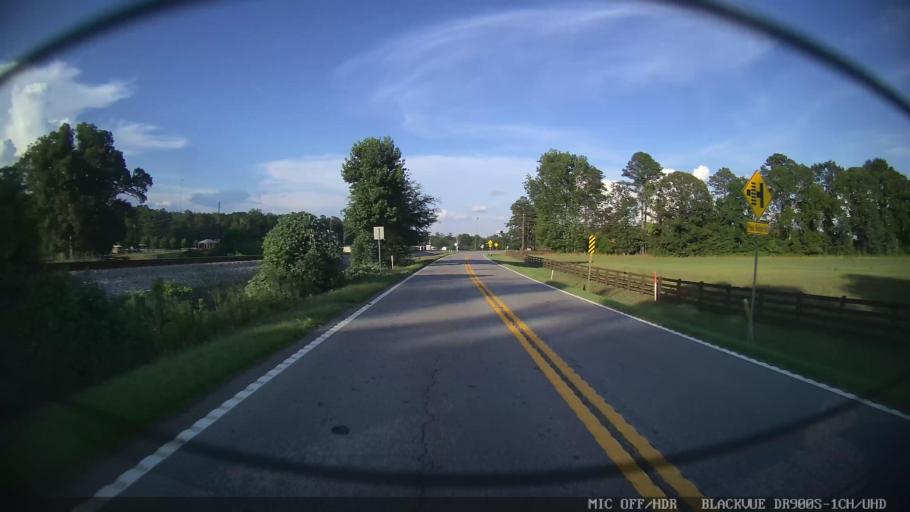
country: US
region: Georgia
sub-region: Monroe County
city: Forsyth
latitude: 32.9509
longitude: -83.8305
